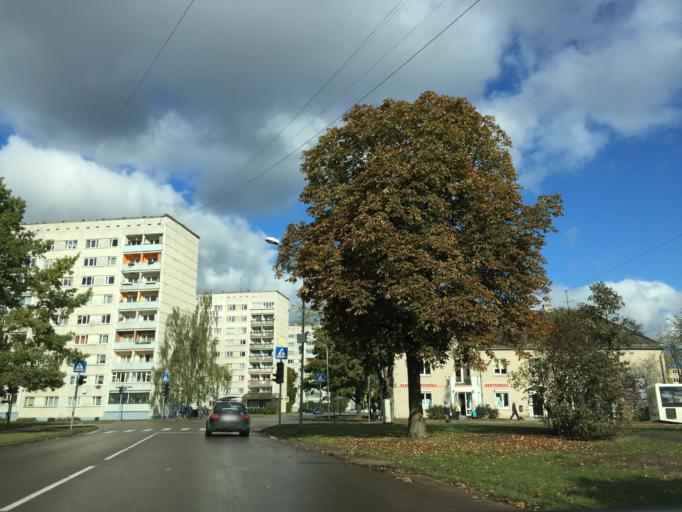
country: LV
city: Tireli
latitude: 56.9588
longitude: 23.6027
